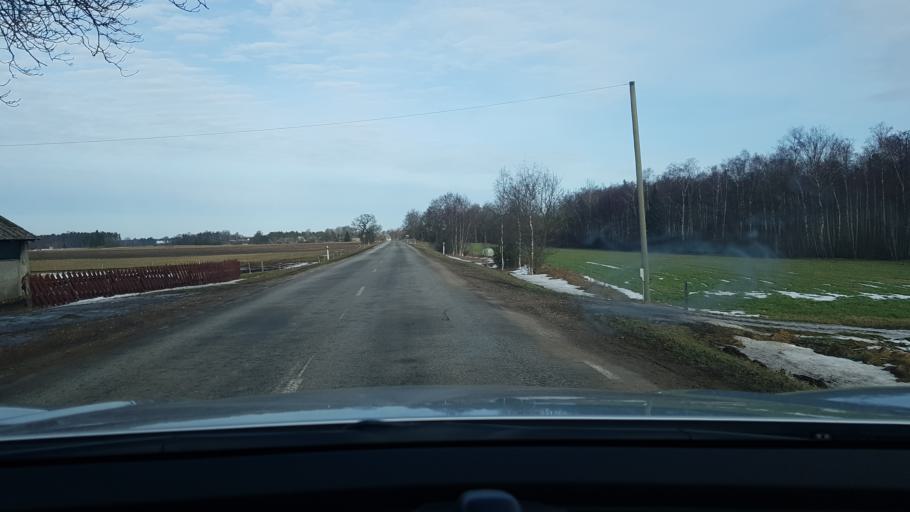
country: EE
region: Saare
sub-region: Kuressaare linn
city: Kuressaare
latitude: 58.4977
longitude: 22.7066
